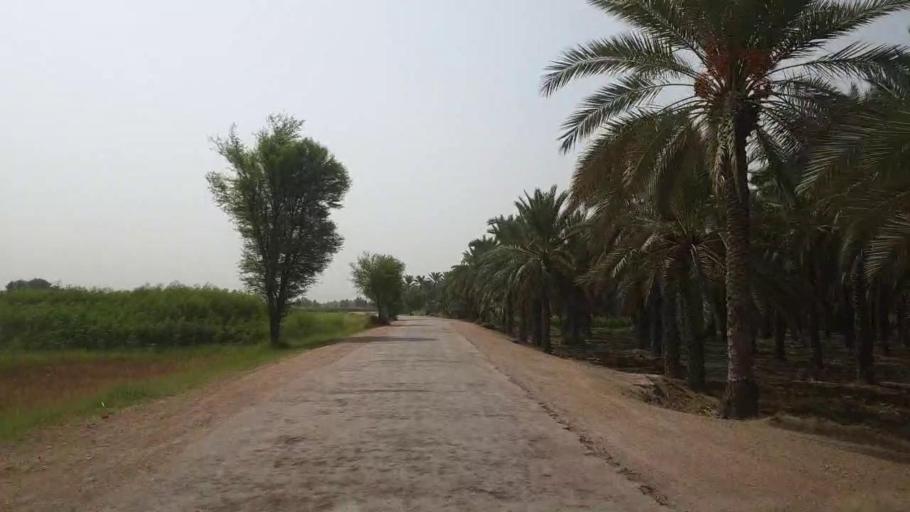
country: PK
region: Sindh
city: Gambat
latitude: 27.4294
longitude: 68.5352
